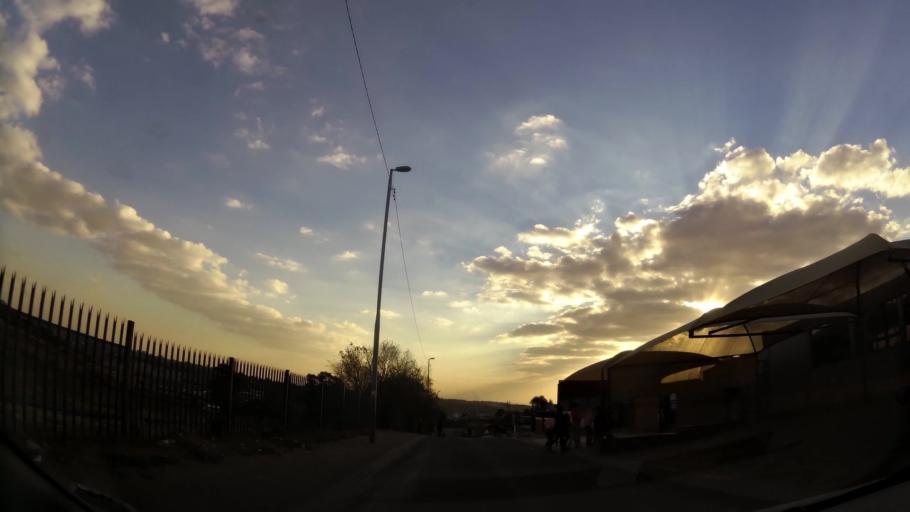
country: ZA
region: Gauteng
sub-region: West Rand District Municipality
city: Krugersdorp
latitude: -26.0822
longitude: 27.7545
